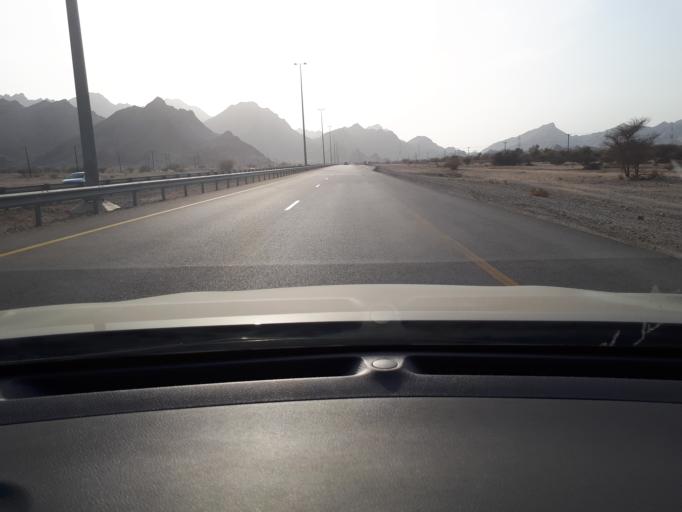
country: OM
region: Muhafazat Masqat
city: Muscat
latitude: 23.3660
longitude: 58.6535
